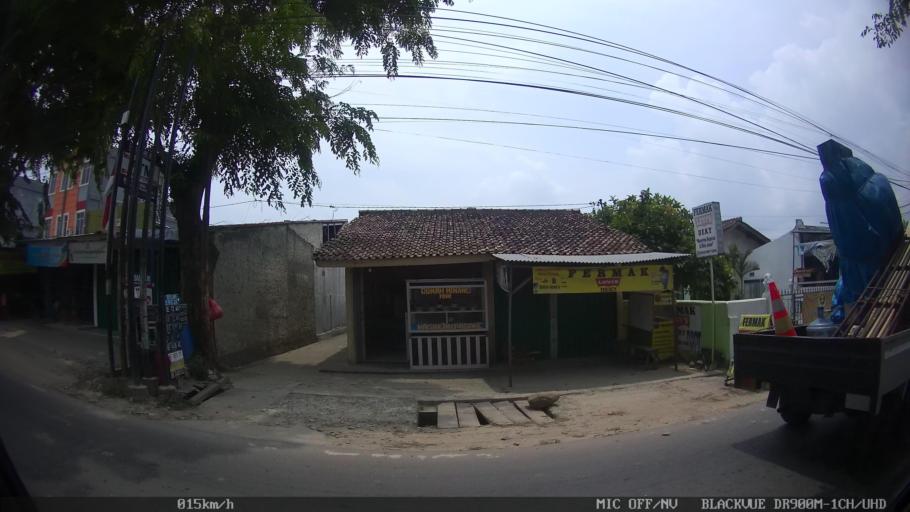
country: ID
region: Lampung
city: Kedaton
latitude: -5.3970
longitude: 105.3020
